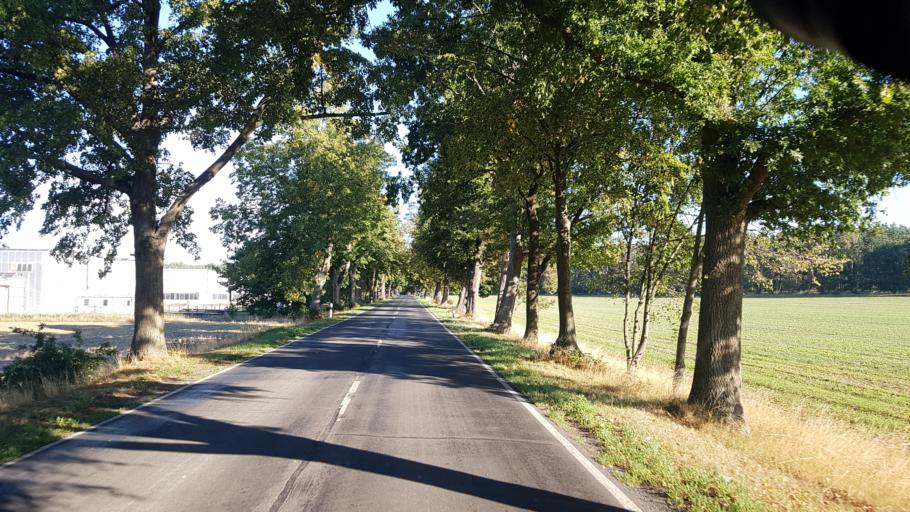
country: DE
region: Brandenburg
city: Bronkow
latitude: 51.6570
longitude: 13.9208
